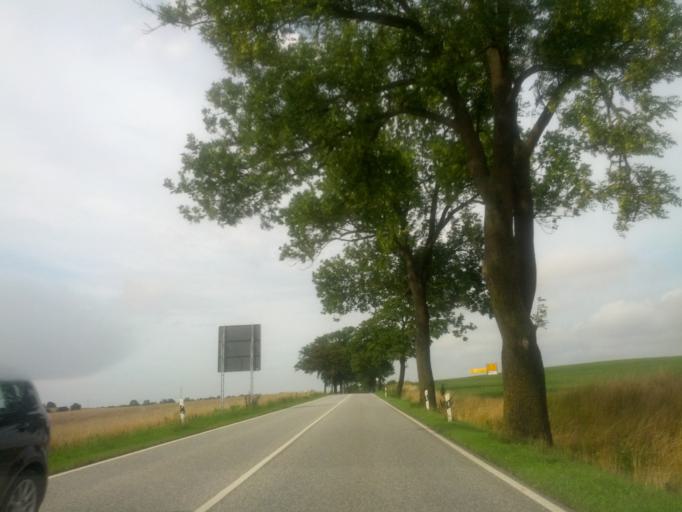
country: DE
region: Mecklenburg-Vorpommern
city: Sellin
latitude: 53.9444
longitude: 11.6128
